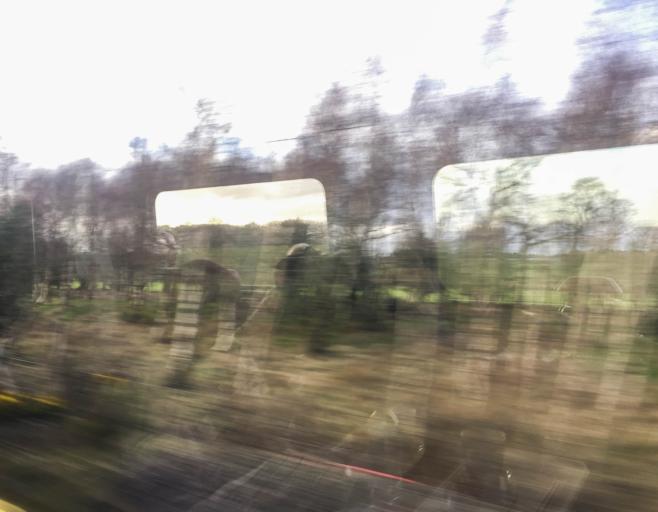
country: GB
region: Scotland
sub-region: Dumfries and Galloway
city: Gretna
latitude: 55.0212
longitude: -3.1120
